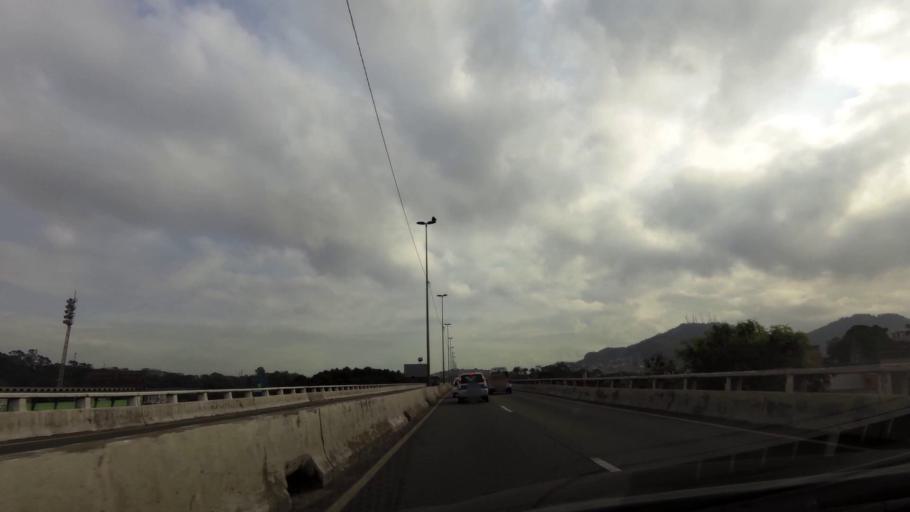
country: BR
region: Espirito Santo
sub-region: Vitoria
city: Vitoria
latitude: -20.3344
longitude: -40.3547
